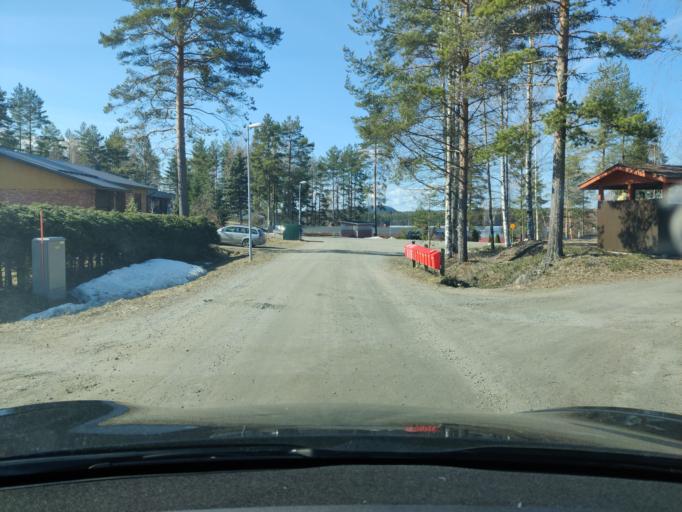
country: FI
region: Northern Savo
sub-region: Kuopio
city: Vehmersalmi
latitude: 62.7590
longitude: 28.0346
